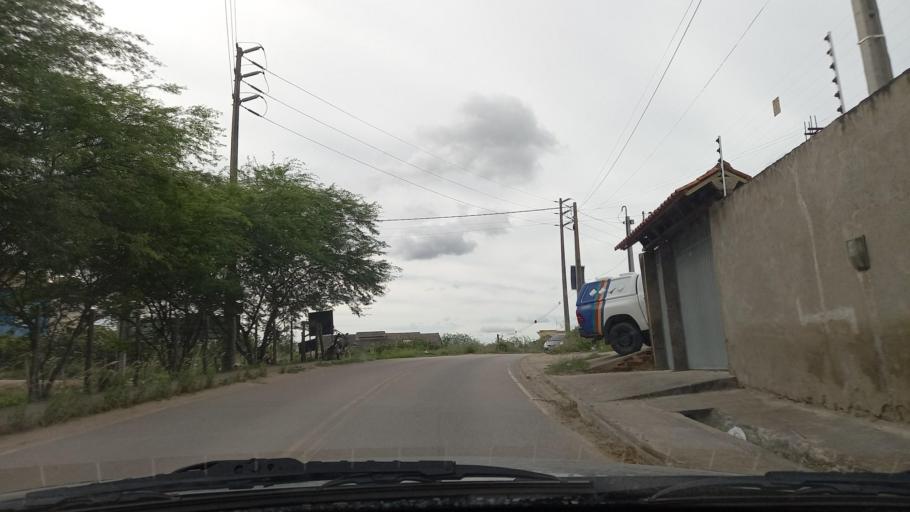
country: BR
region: Pernambuco
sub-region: Gravata
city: Gravata
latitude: -8.2147
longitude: -35.5796
